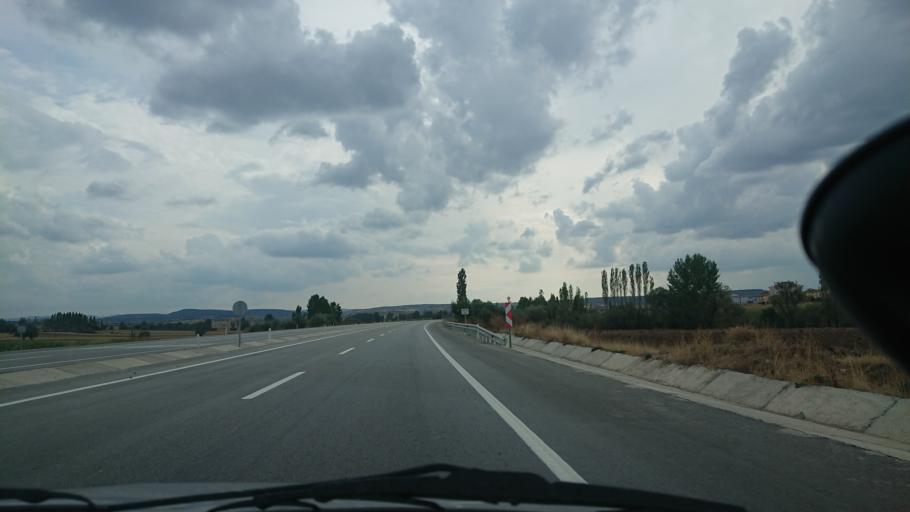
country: TR
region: Kuetahya
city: Cavdarhisar
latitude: 39.1865
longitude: 29.6190
